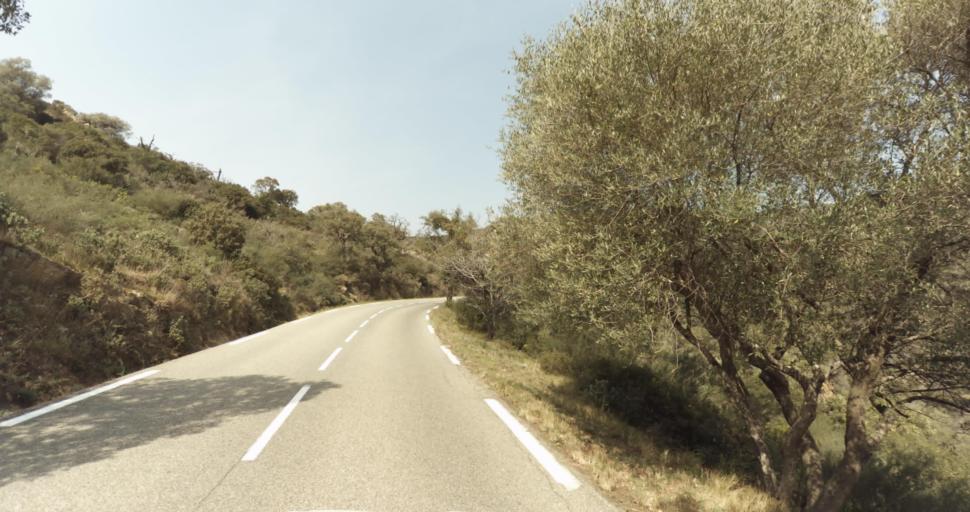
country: FR
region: Provence-Alpes-Cote d'Azur
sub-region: Departement du Var
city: Bormes-les-Mimosas
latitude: 43.1587
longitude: 6.3439
